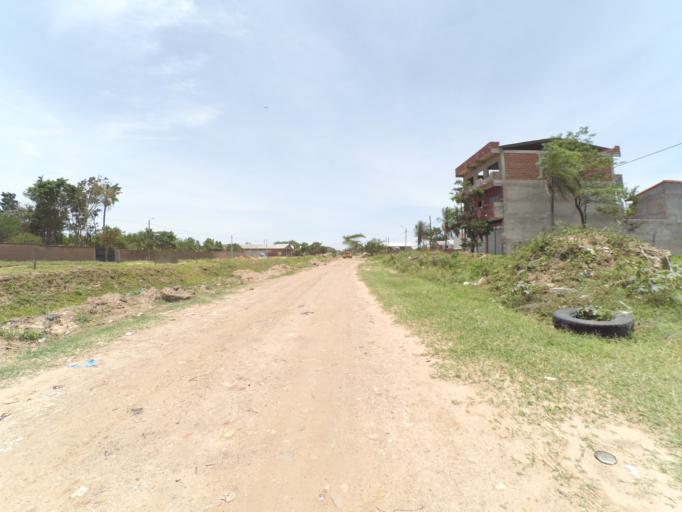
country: BO
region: Santa Cruz
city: Santa Cruz de la Sierra
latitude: -17.8239
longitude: -63.2463
